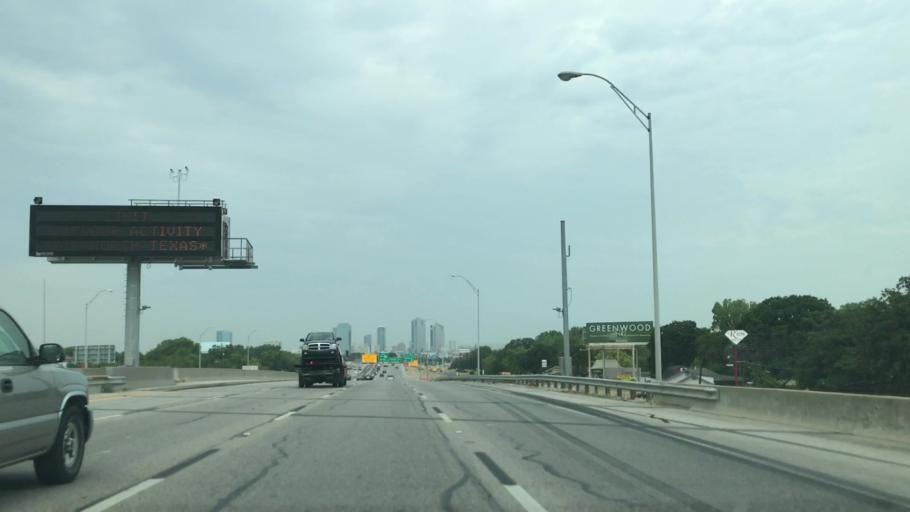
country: US
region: Texas
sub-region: Tarrant County
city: Haltom City
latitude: 32.7716
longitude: -97.2952
